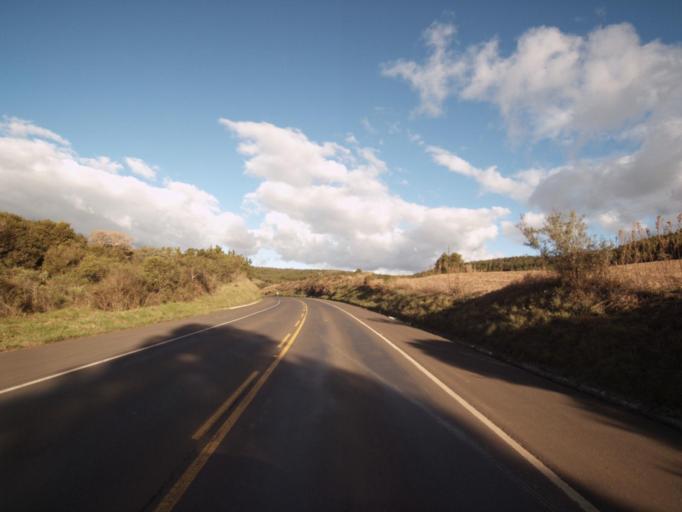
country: BR
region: Santa Catarina
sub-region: Campos Novos
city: Campos Novos
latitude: -27.3576
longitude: -51.3308
